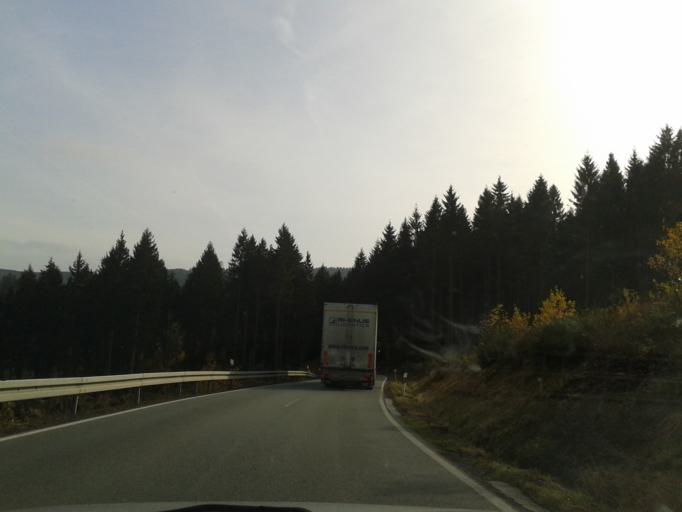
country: DE
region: North Rhine-Westphalia
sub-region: Regierungsbezirk Arnsberg
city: Bestwig
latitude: 51.3906
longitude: 8.4170
